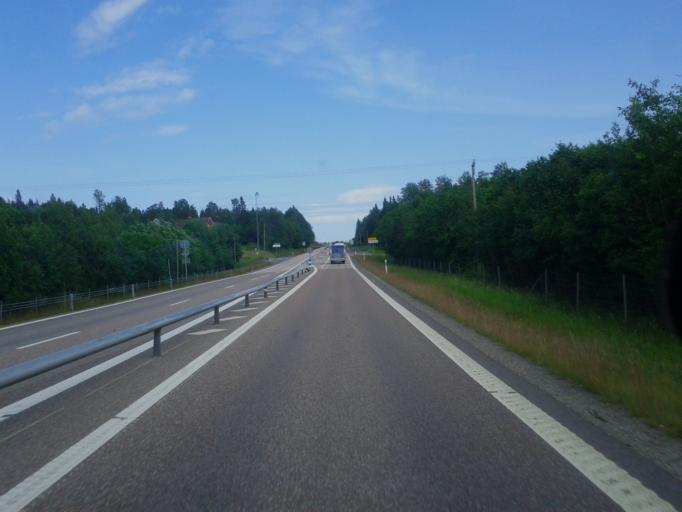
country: SE
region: Vaesternorrland
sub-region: OErnskoeldsviks Kommun
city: Husum
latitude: 63.3610
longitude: 19.1759
